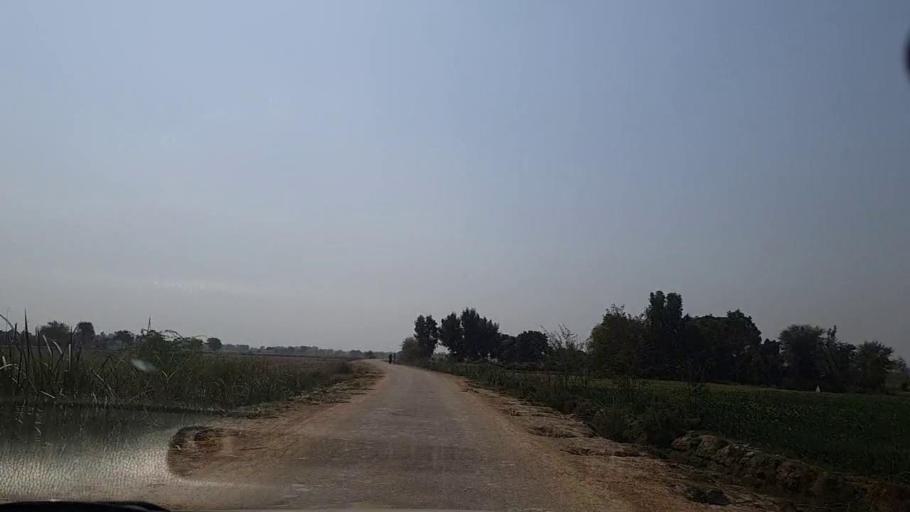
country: PK
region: Sindh
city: Mirpur Khas
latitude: 25.4853
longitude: 69.1941
